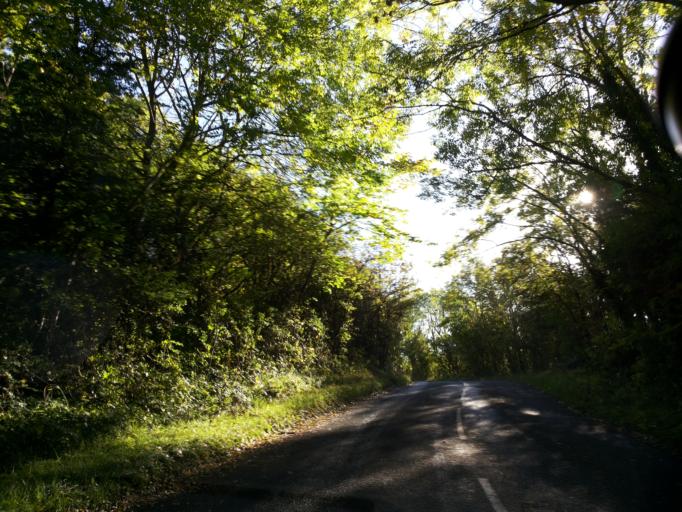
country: GB
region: England
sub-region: North Yorkshire
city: Catterick Garrison
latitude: 54.4373
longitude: -1.7666
